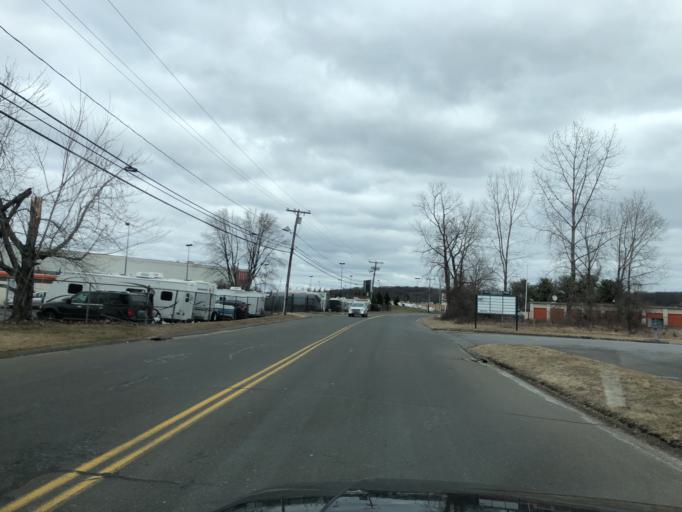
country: US
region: Connecticut
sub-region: Hartford County
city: Plainville
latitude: 41.6330
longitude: -72.8792
